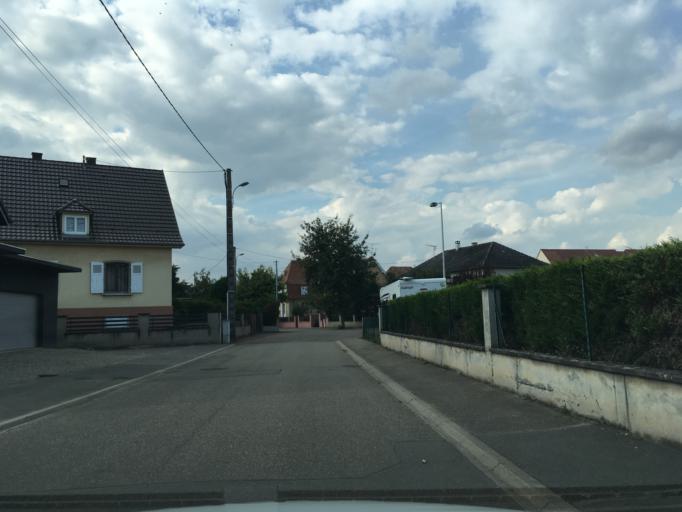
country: FR
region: Alsace
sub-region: Departement du Haut-Rhin
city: Colmar
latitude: 48.0700
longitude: 7.3691
